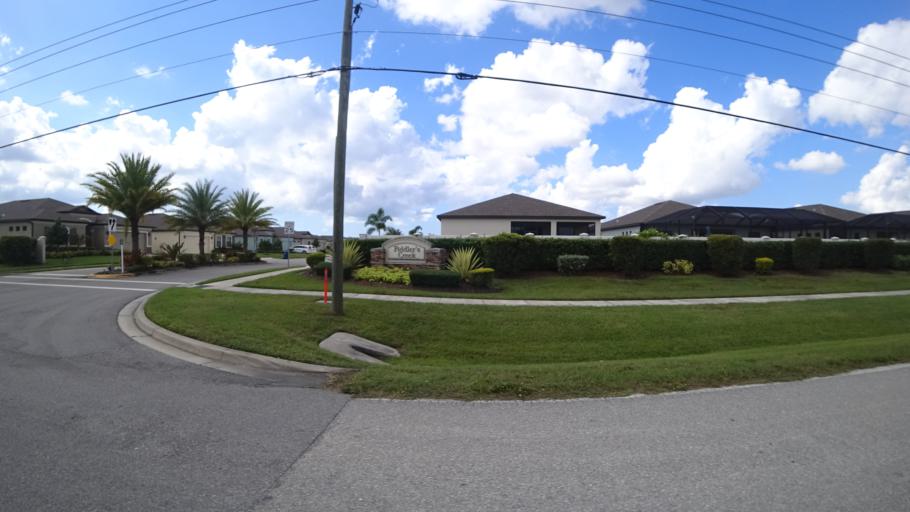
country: US
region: Florida
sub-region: Sarasota County
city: North Sarasota
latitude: 27.4210
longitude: -82.5177
